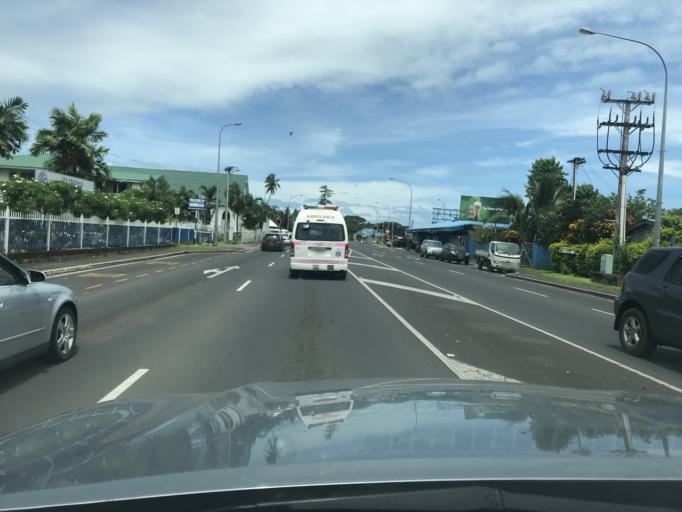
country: WS
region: Tuamasaga
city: Apia
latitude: -13.8387
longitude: -171.7763
